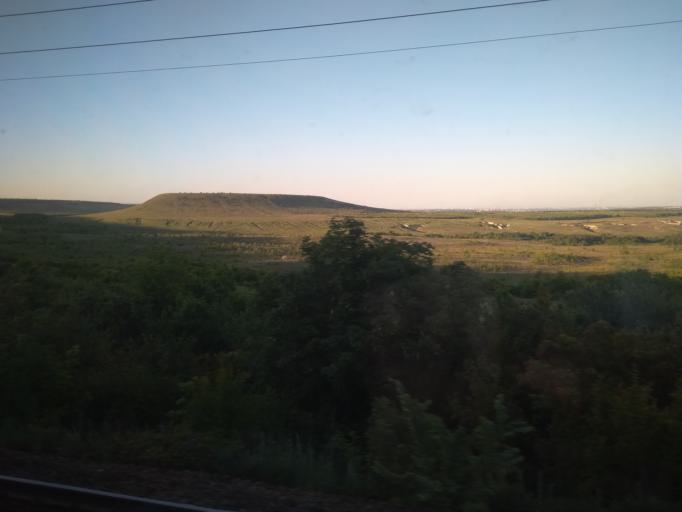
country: RU
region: Saratov
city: Krasnyy Oktyabr'
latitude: 51.4272
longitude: 45.7727
